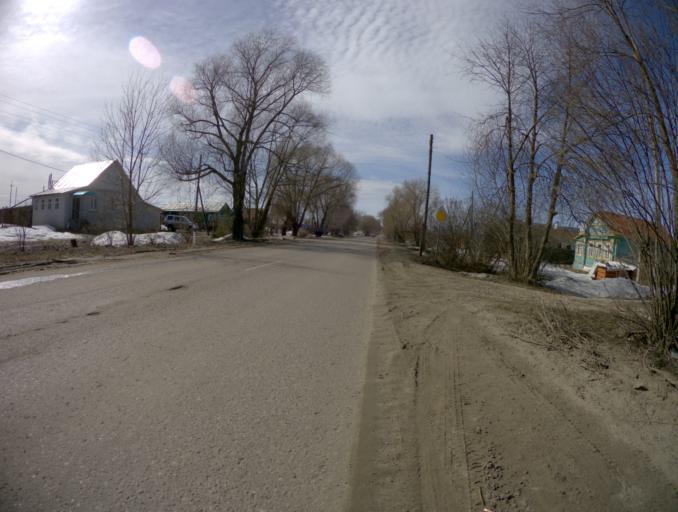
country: RU
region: Vladimir
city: Suzdal'
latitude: 56.4271
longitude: 40.4242
